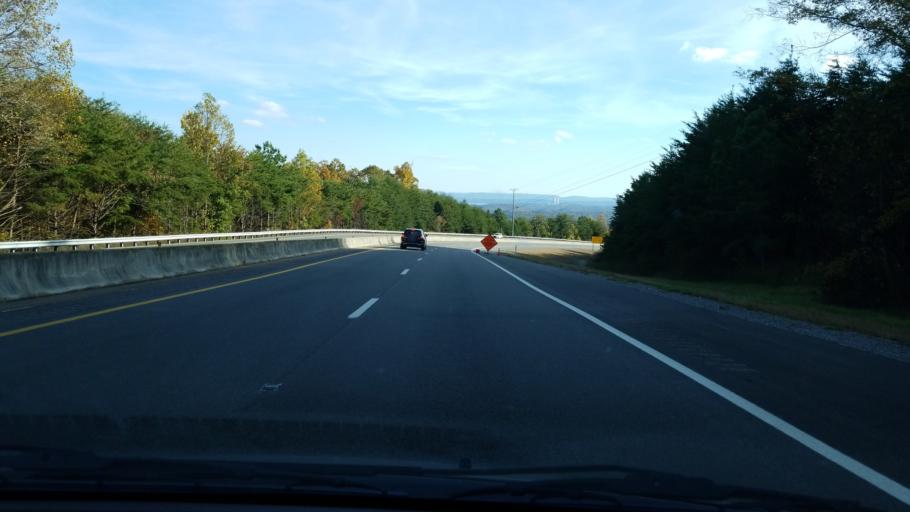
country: US
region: Tennessee
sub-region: Hamilton County
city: Sale Creek
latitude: 35.3256
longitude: -85.1618
